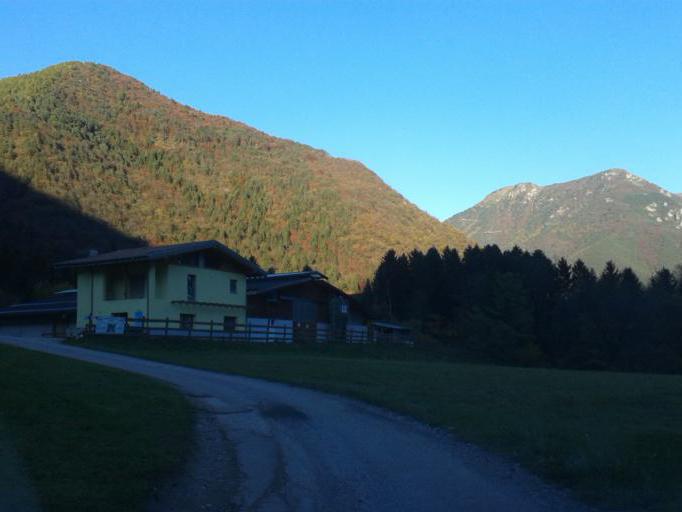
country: IT
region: Trentino-Alto Adige
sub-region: Provincia di Trento
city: Pieve di Ledro
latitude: 45.8947
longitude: 10.7047
